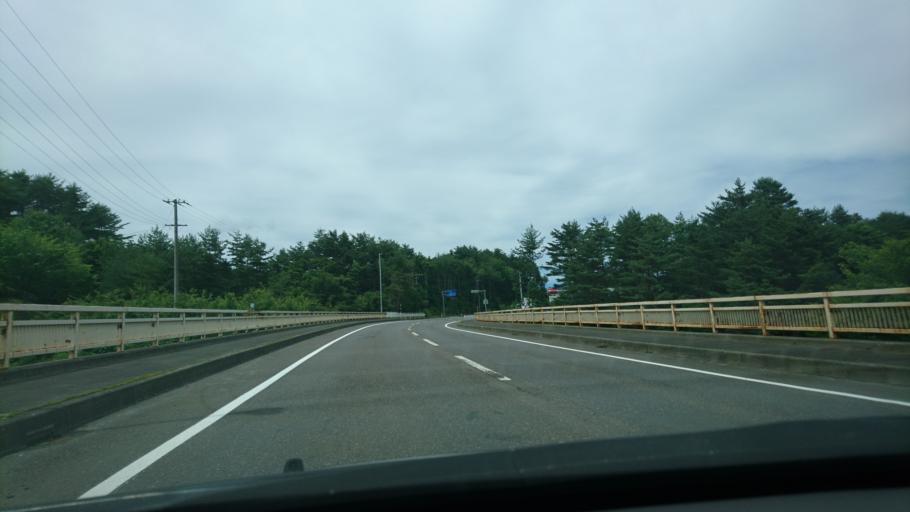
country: JP
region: Iwate
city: Miyako
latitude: 39.9102
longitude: 141.9027
